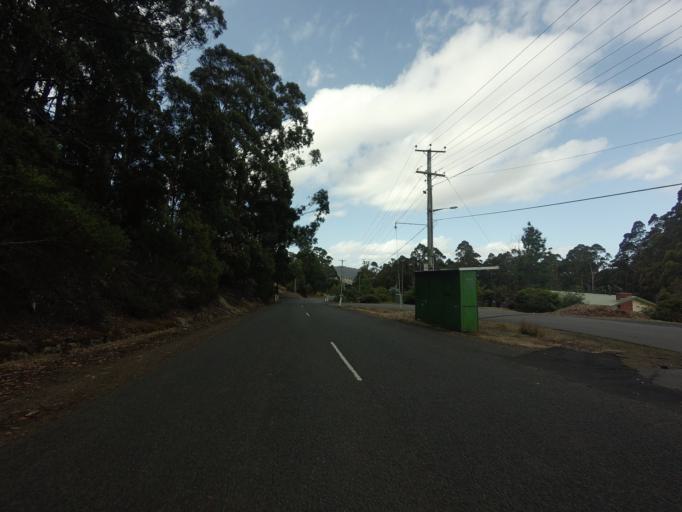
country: AU
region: Tasmania
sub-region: Hobart
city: Dynnyrne
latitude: -42.9059
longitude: 147.2678
